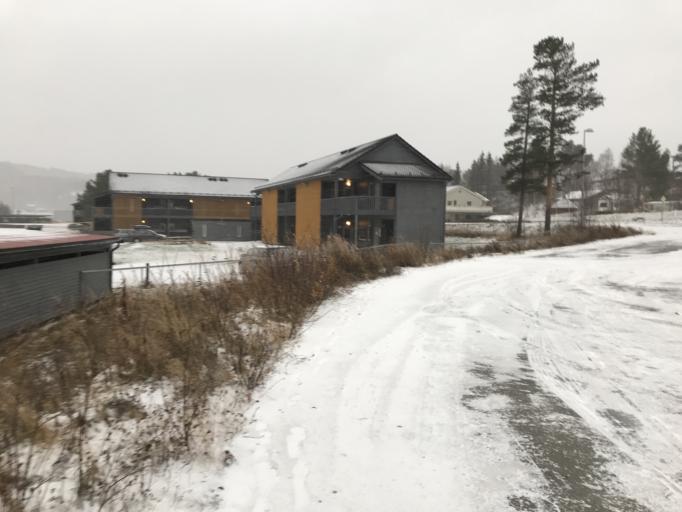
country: NO
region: Troms
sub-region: Balsfjord
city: Storsteinnes
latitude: 69.0249
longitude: 19.2952
